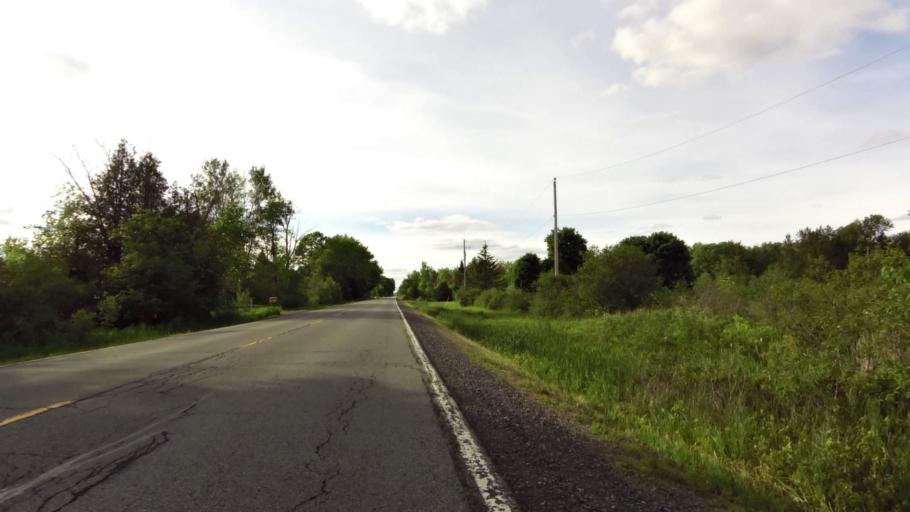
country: CA
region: Ontario
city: Ottawa
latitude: 45.2089
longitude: -75.5963
